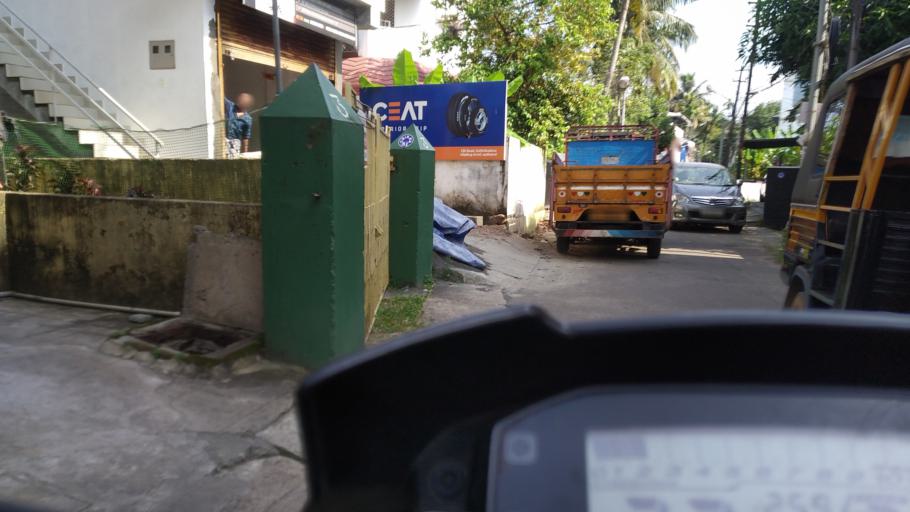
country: IN
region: Kerala
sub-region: Ernakulam
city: Cochin
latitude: 9.9828
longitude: 76.2932
